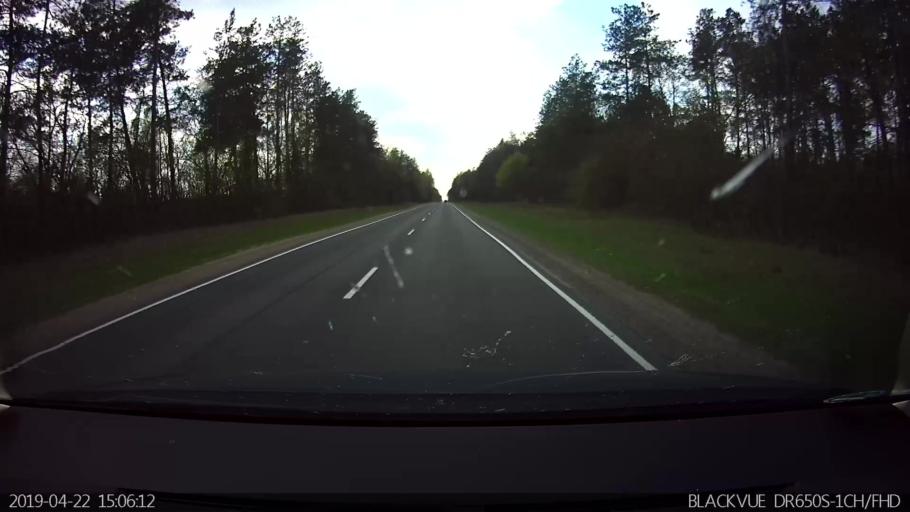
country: BY
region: Brest
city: Kamyanyets
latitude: 52.3322
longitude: 23.8442
